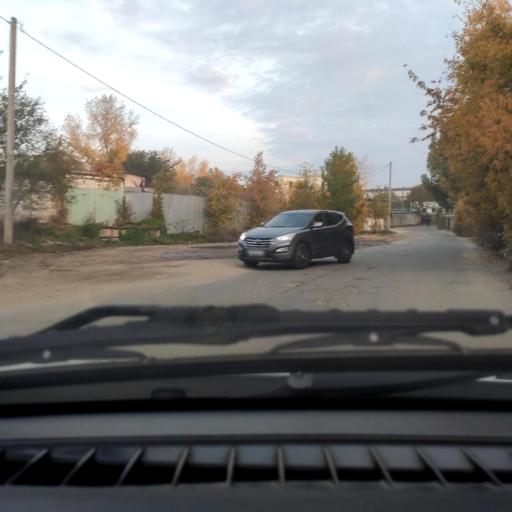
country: RU
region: Samara
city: Zhigulevsk
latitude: 53.4848
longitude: 49.4917
